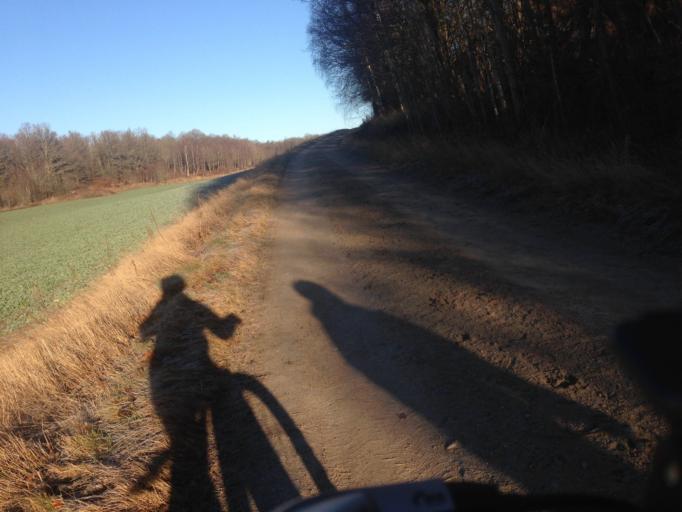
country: SE
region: Blekinge
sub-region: Karlshamns Kommun
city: Morrum
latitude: 56.1813
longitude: 14.7820
